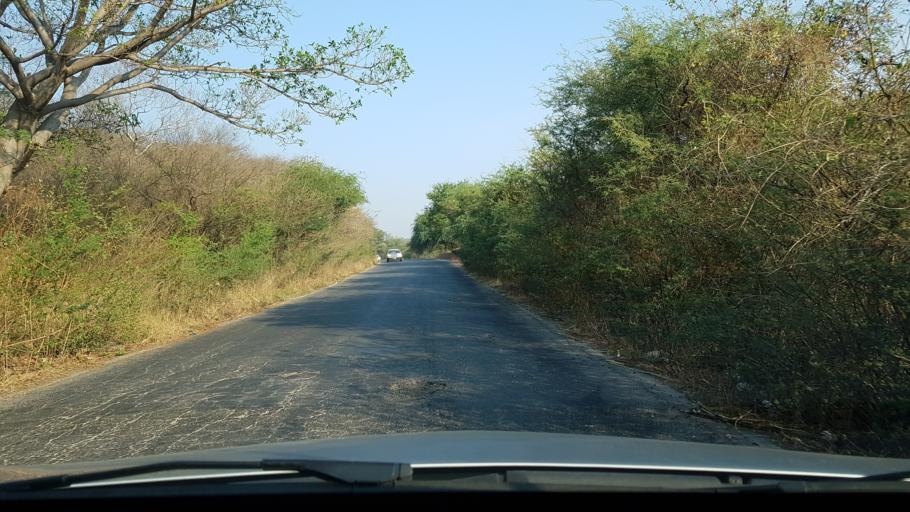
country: MX
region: Morelos
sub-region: Tepalcingo
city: Zacapalco
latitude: 18.6471
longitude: -99.0249
